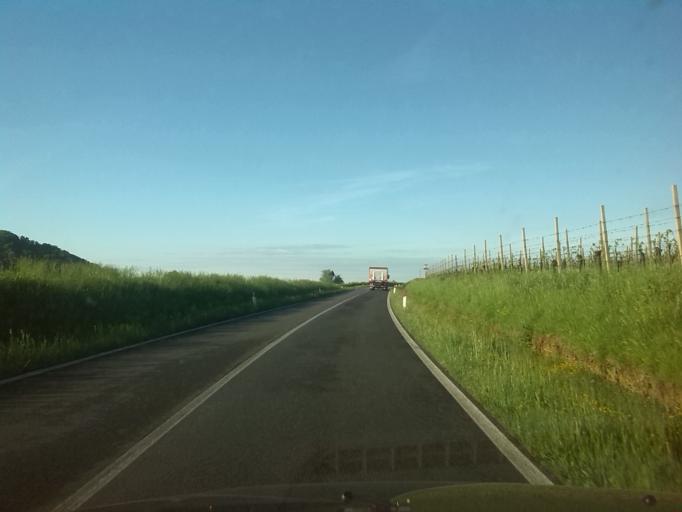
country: IT
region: Friuli Venezia Giulia
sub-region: Provincia di Udine
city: Corno di Rosazzo
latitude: 46.0211
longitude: 13.4402
